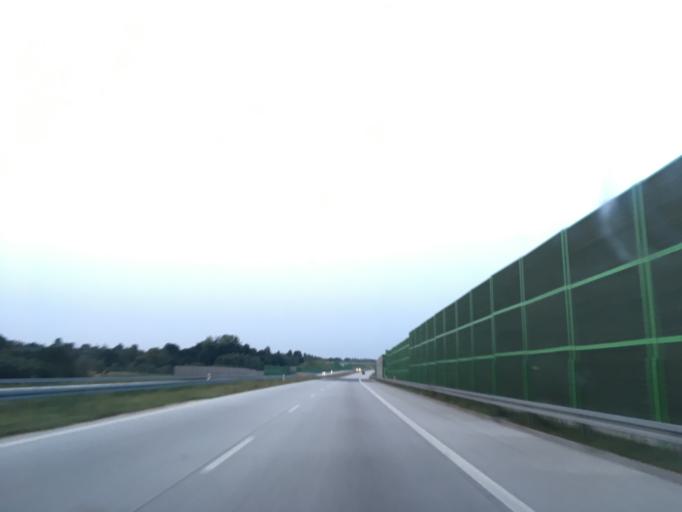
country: PL
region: Lodz Voivodeship
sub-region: Powiat zgierski
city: Strykow
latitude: 51.8275
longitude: 19.6520
